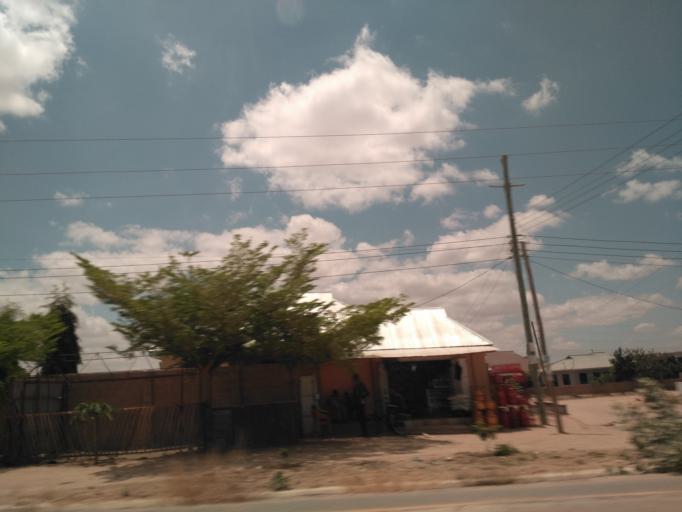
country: TZ
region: Dodoma
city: Kisasa
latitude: -6.1749
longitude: 35.7952
